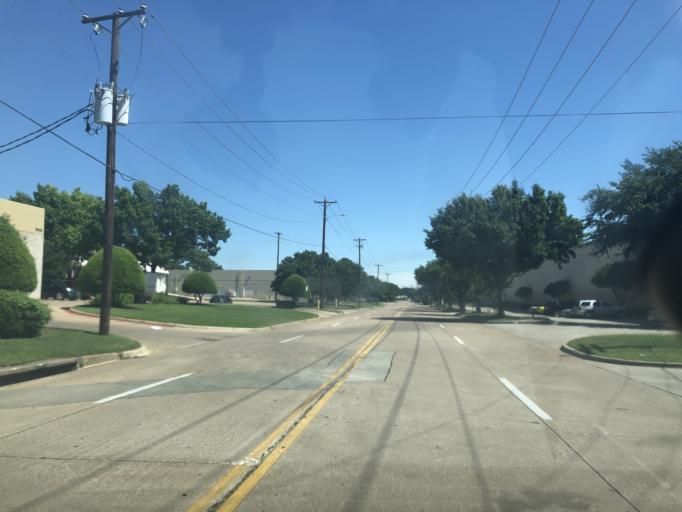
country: US
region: Texas
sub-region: Dallas County
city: Grand Prairie
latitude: 32.7915
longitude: -97.0396
